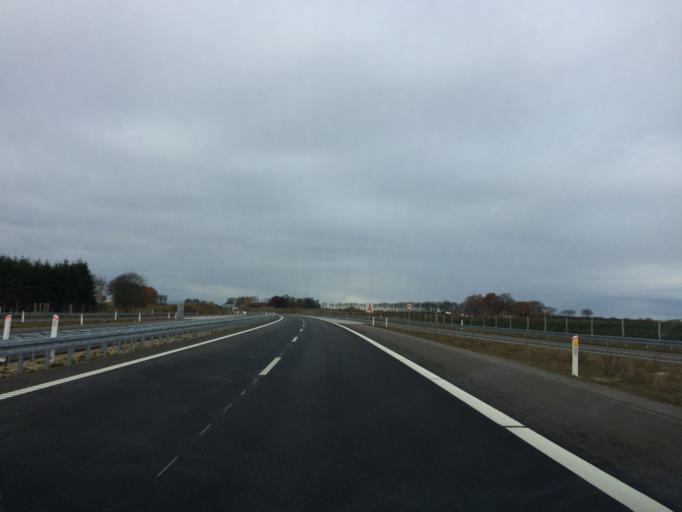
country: DK
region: Central Jutland
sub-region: Silkeborg Kommune
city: Silkeborg
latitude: 56.2019
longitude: 9.5485
